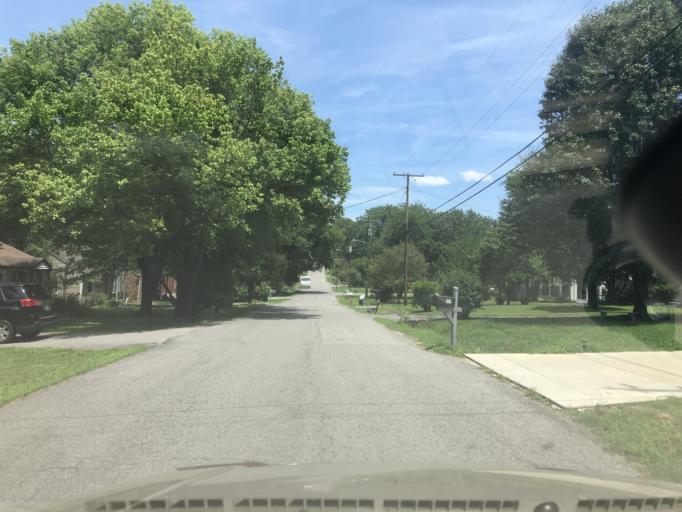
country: US
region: Tennessee
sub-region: Davidson County
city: Lakewood
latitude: 36.2574
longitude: -86.6994
